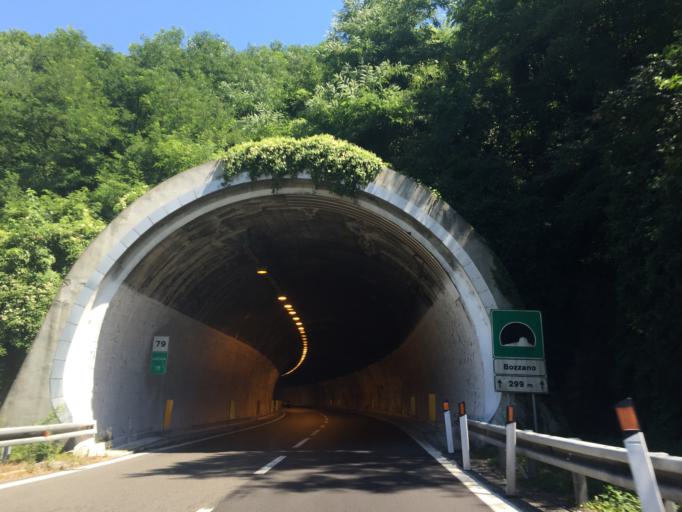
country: IT
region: Tuscany
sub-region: Provincia di Lucca
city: Massarosa
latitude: 43.8711
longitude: 10.3515
